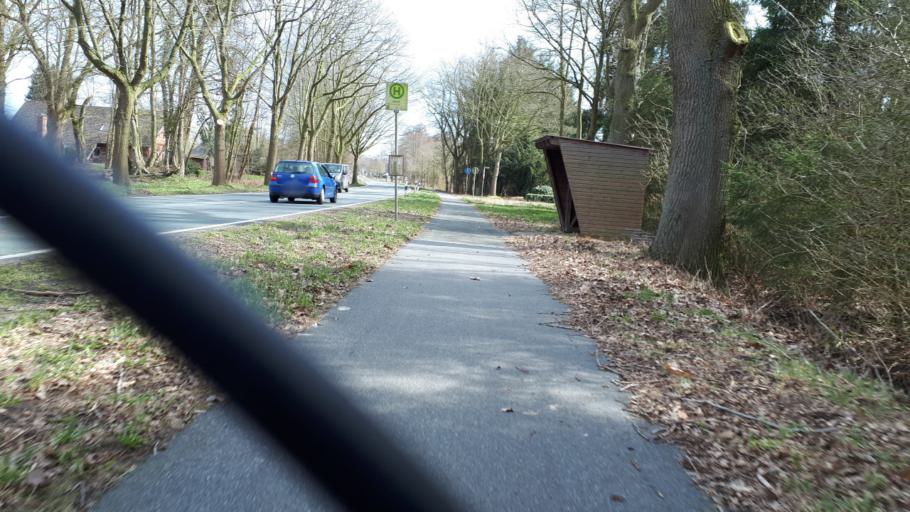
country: DE
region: Lower Saxony
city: Hude
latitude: 53.0552
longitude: 8.4693
